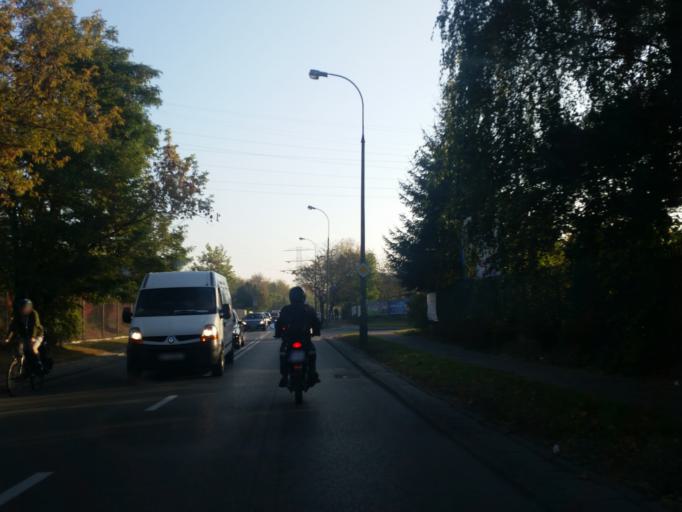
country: PL
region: Masovian Voivodeship
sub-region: Warszawa
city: Mokotow
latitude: 52.1912
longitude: 21.0425
